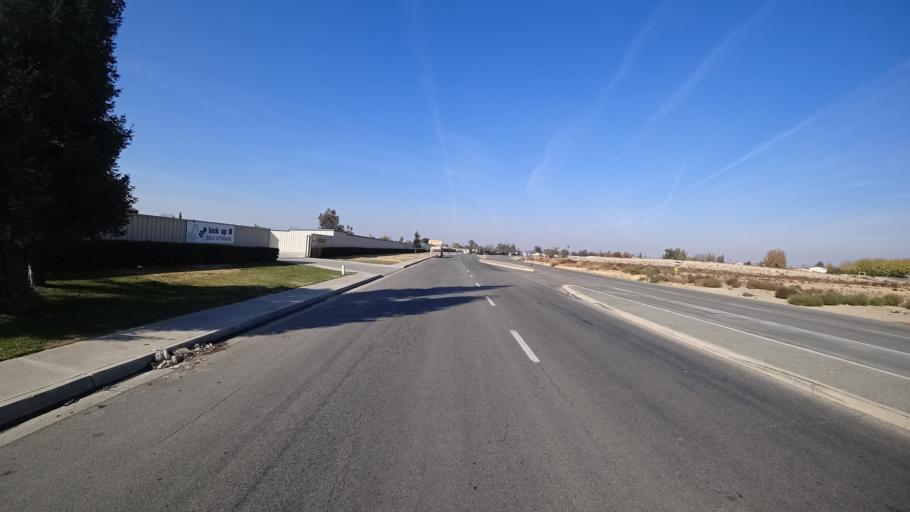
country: US
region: California
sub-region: Kern County
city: Greenfield
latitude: 35.3203
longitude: -119.0057
